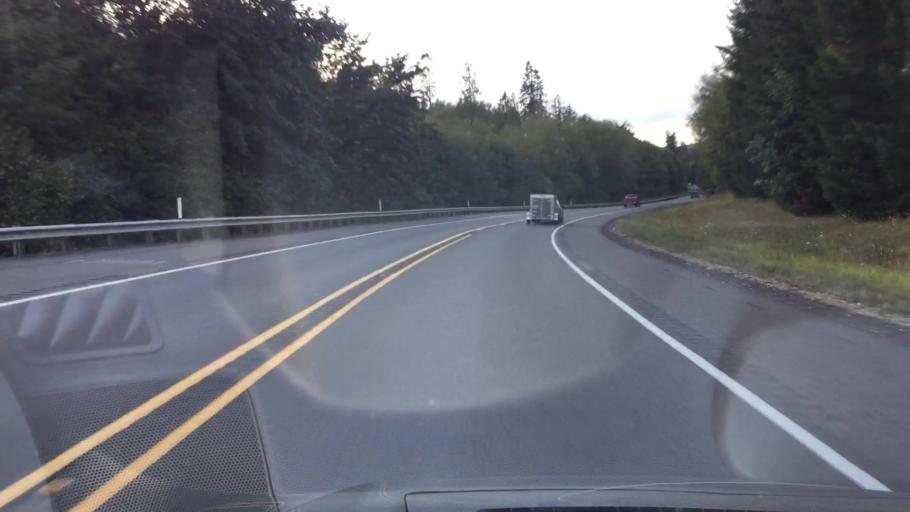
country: US
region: Washington
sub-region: Lewis County
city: Morton
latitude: 46.5326
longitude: -122.5364
